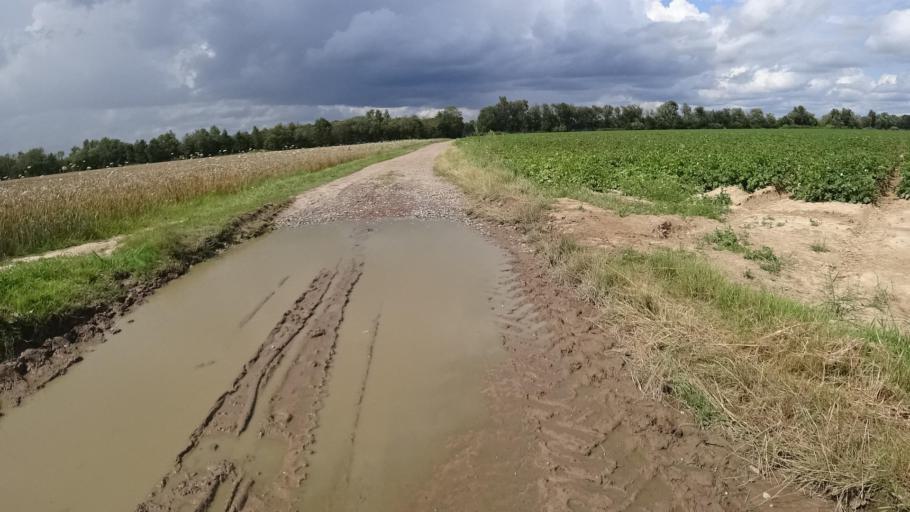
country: BE
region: Wallonia
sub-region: Province de Namur
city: Sombreffe
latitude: 50.5693
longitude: 4.5727
